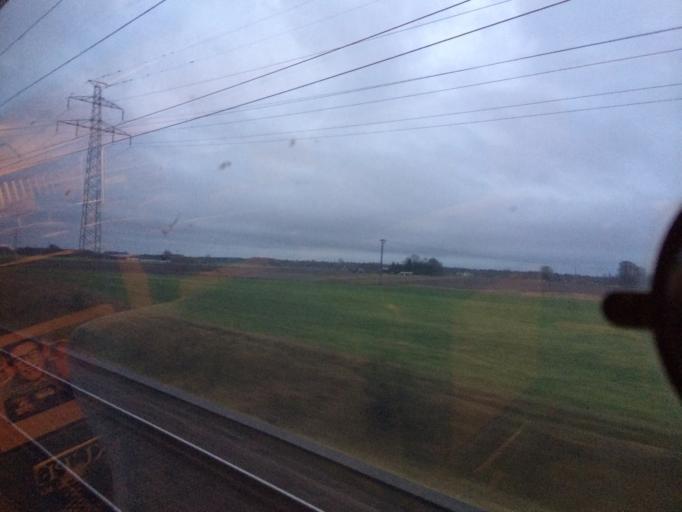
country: SE
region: Skane
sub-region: Kavlinge Kommun
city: Hofterup
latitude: 55.8345
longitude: 12.9842
